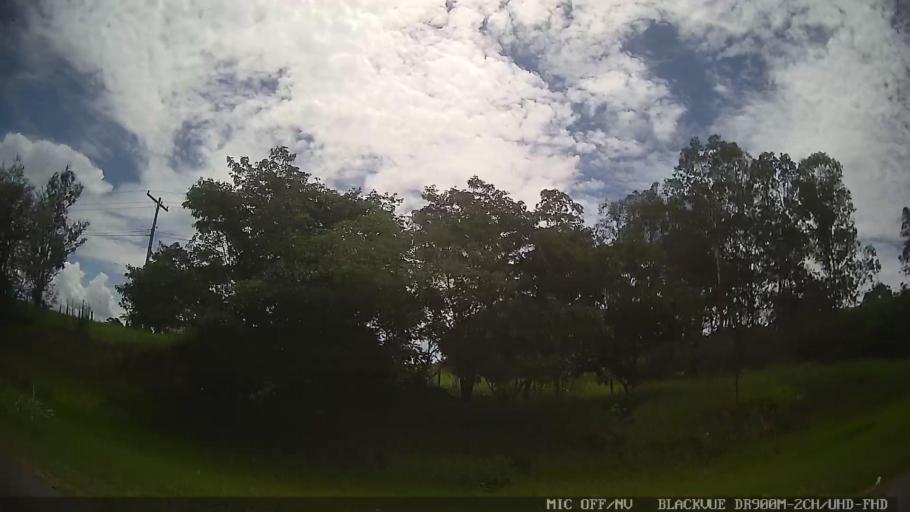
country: BR
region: Sao Paulo
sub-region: Conchas
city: Conchas
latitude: -23.0543
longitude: -47.9600
